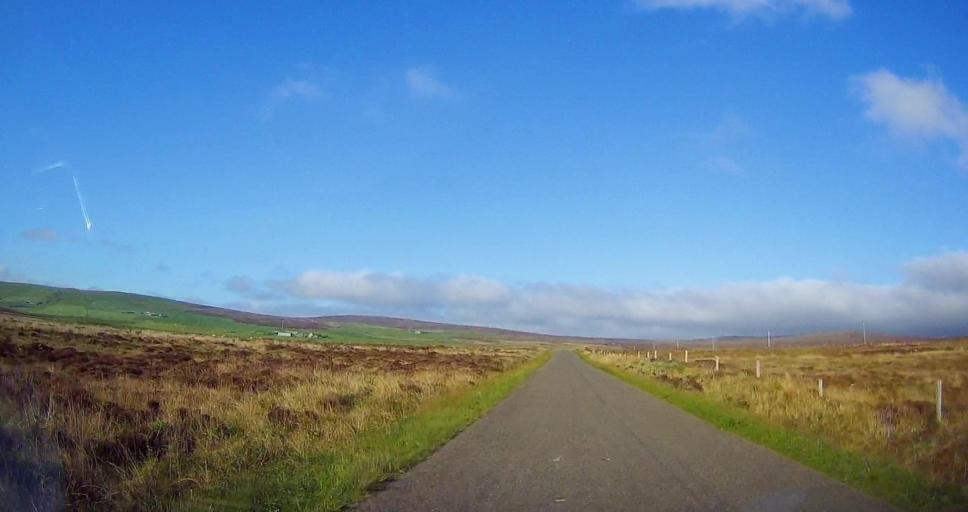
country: GB
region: Scotland
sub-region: Orkney Islands
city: Stromness
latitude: 59.0805
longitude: -3.1956
